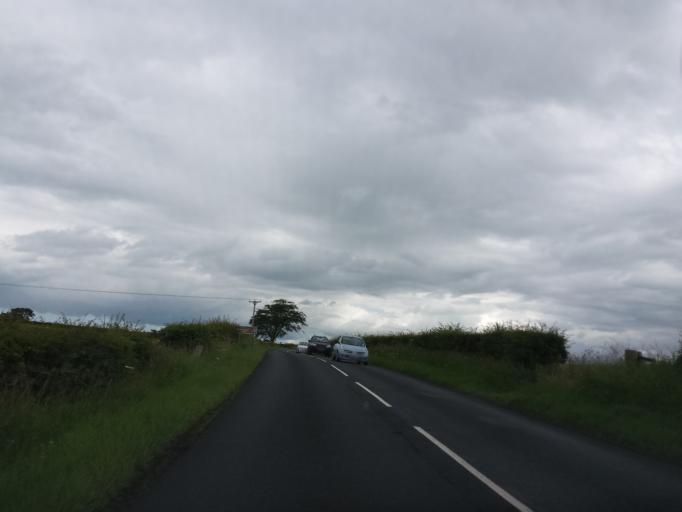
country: GB
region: Scotland
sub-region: The Scottish Borders
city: Saint Boswells
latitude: 55.6000
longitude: -2.5563
